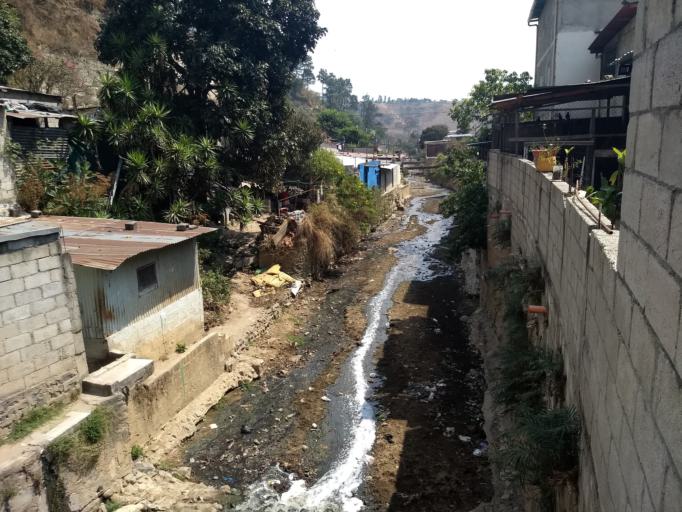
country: GT
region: Guatemala
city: Villa Nueva
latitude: 14.5476
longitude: -90.5842
